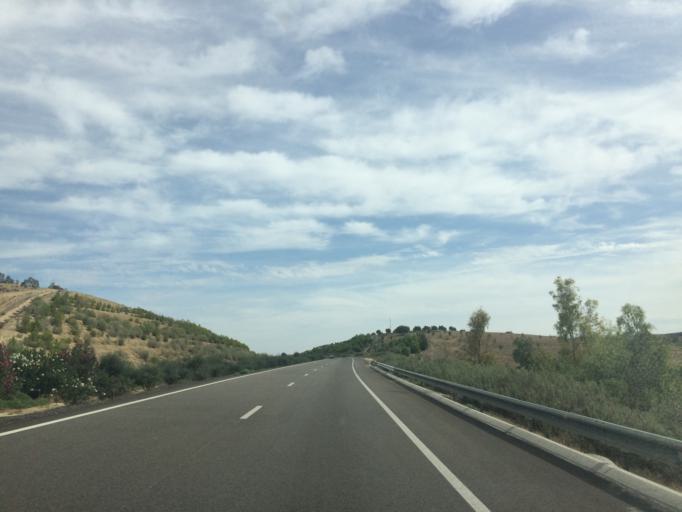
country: MA
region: Rabat-Sale-Zemmour-Zaer
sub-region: Khemisset
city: Khemisset
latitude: 33.8321
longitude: -5.8475
